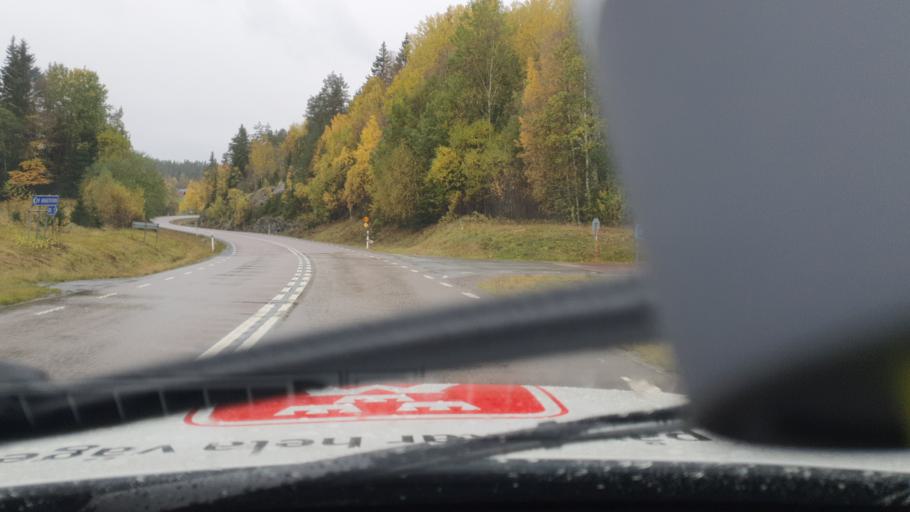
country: SE
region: Vaestra Goetaland
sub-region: Dals-Ed Kommun
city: Ed
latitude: 58.9194
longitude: 12.0229
